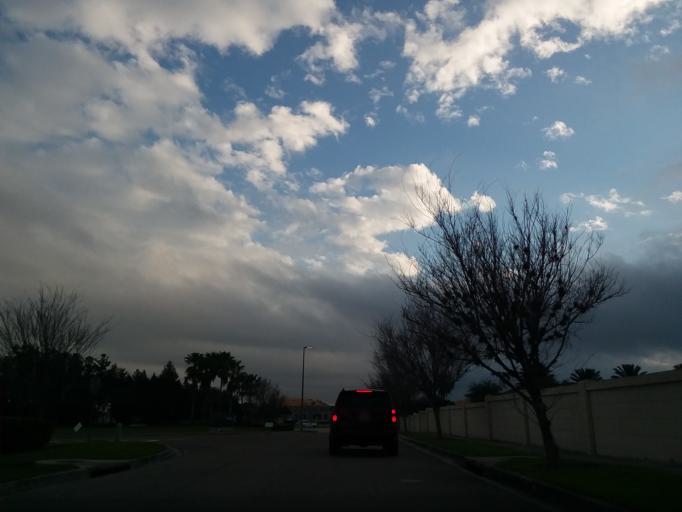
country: US
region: Florida
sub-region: Osceola County
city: Poinciana
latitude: 28.1808
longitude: -81.4379
